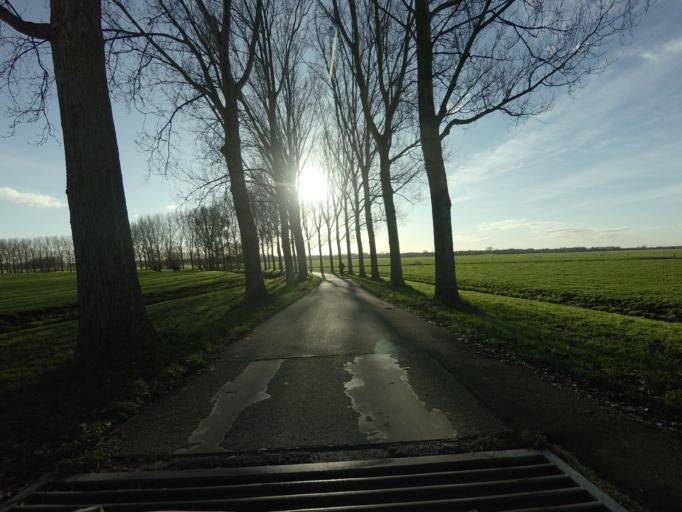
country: NL
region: South Holland
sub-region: Gemeente Alphen aan den Rijn
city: Alphen aan den Rijn
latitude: 52.1611
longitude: 4.6953
